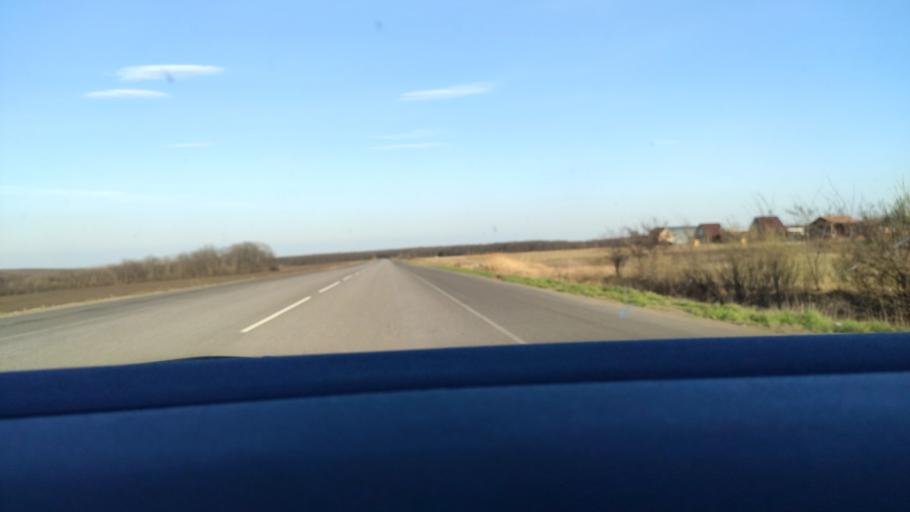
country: RU
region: Voronezj
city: Kolodeznyy
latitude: 51.3403
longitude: 39.0396
